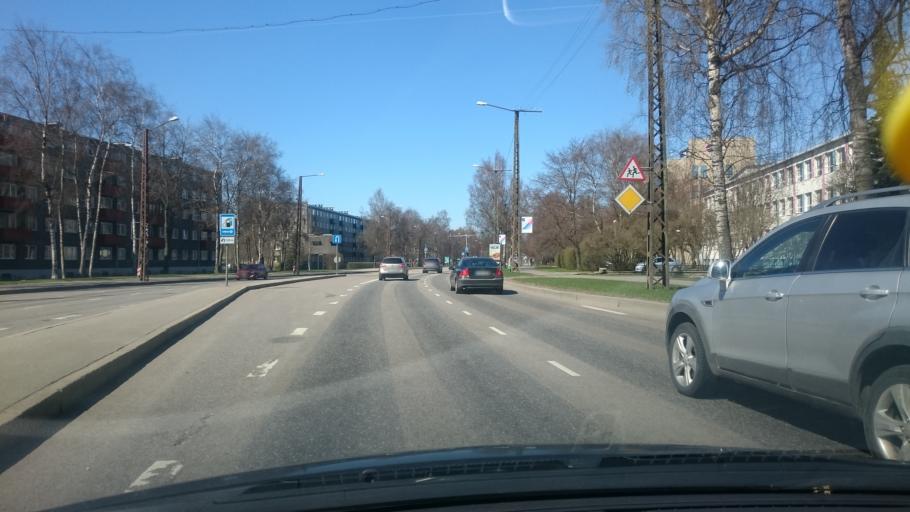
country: EE
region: Harju
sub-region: Tallinna linn
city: Tallinn
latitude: 59.4333
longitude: 24.7151
